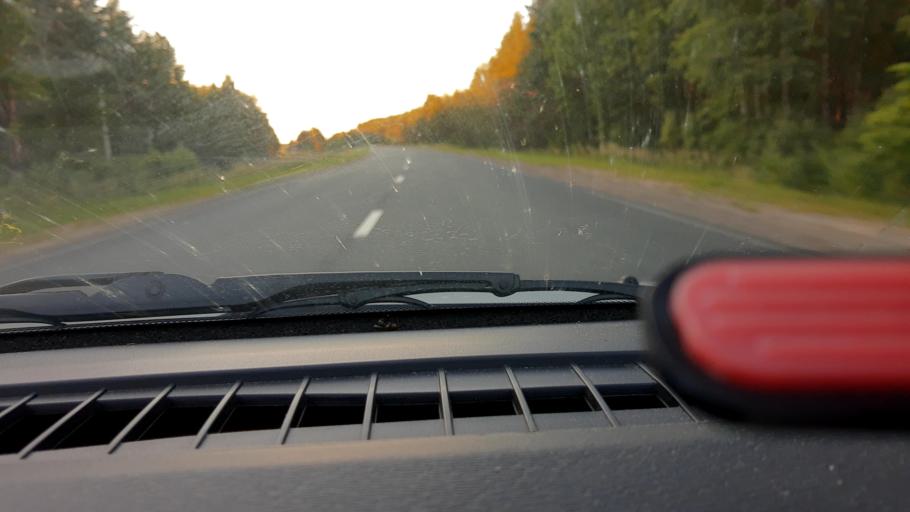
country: RU
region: Nizjnij Novgorod
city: Uren'
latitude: 57.3931
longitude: 45.6872
